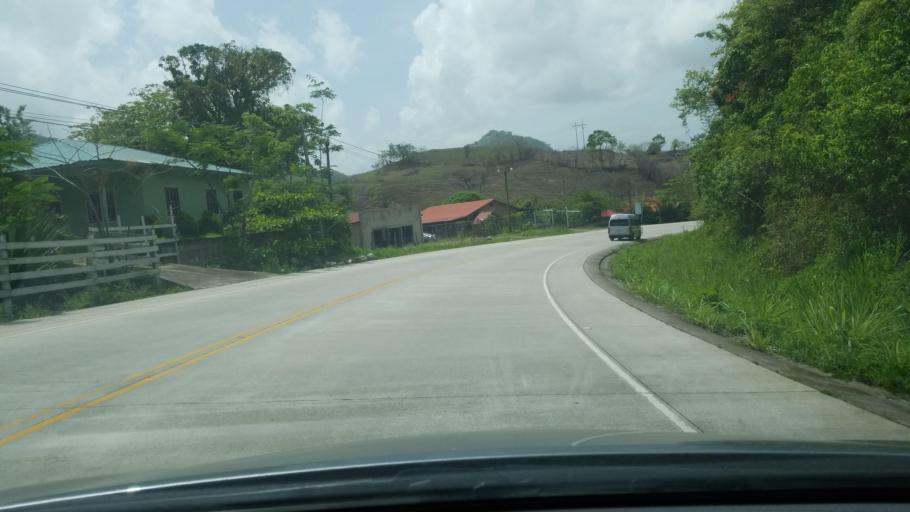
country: HN
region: Copan
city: San Juan de Planes
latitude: 14.9672
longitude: -88.7799
